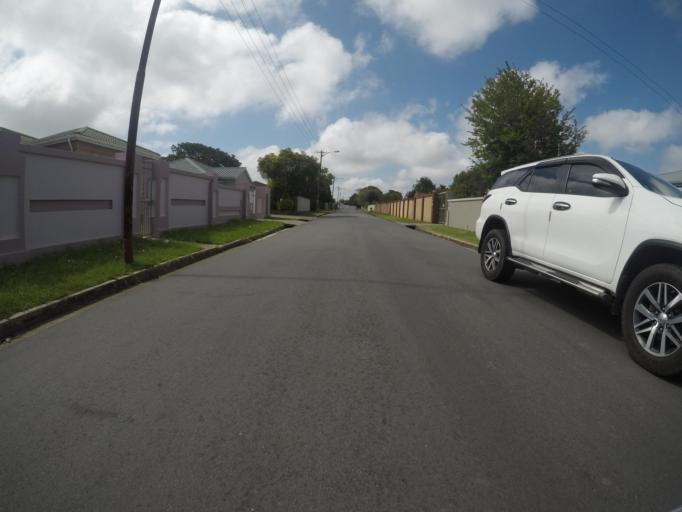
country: ZA
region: Eastern Cape
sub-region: Buffalo City Metropolitan Municipality
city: East London
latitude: -32.9805
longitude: 27.9081
